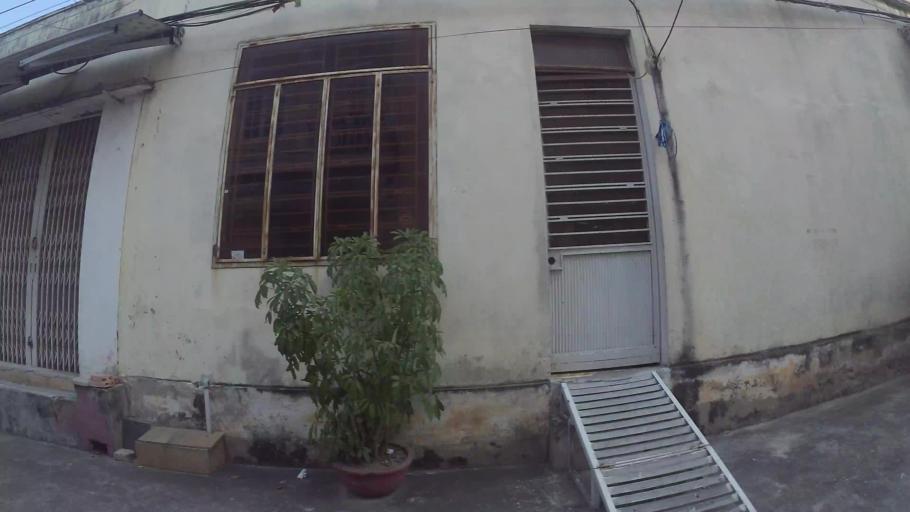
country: VN
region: Da Nang
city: Son Tra
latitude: 16.0438
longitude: 108.2397
